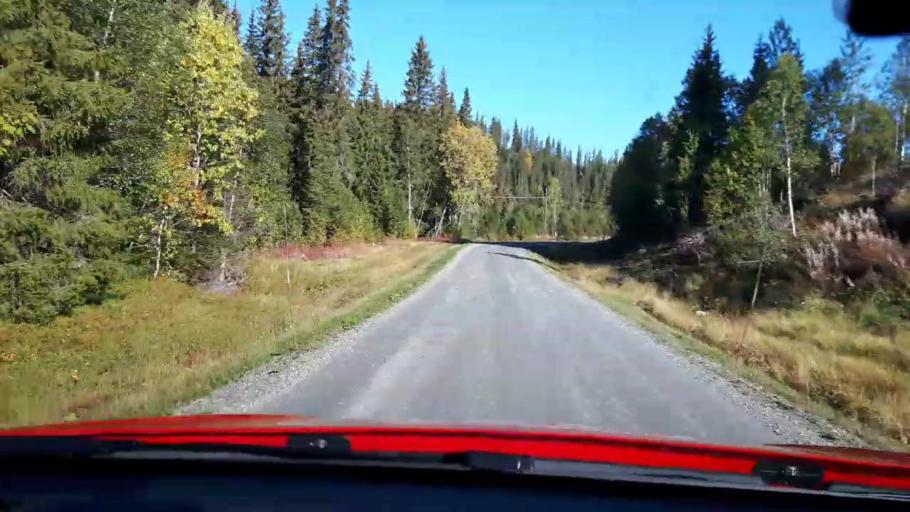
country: NO
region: Nord-Trondelag
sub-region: Lierne
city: Sandvika
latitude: 64.6471
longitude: 13.7461
